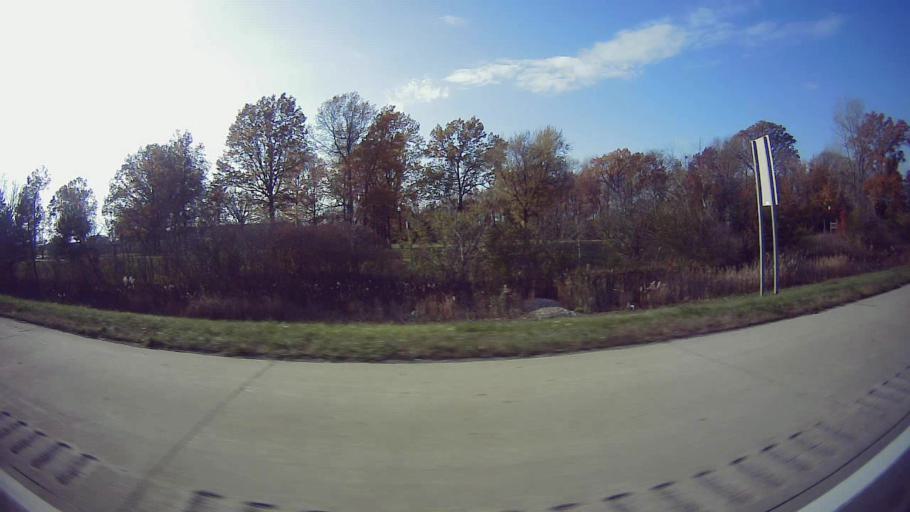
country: US
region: Michigan
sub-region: Wayne County
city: Woodhaven
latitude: 42.1250
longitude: -83.2415
